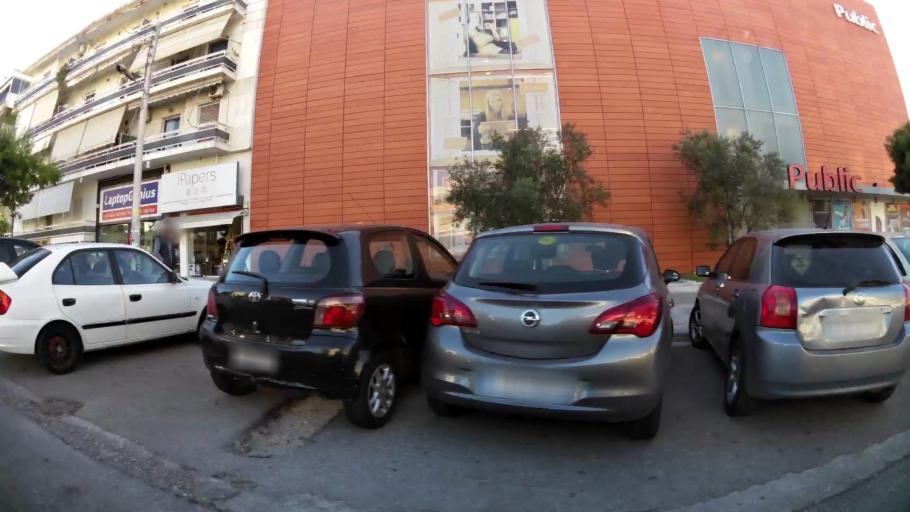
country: GR
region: Attica
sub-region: Nomarchia Athinas
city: Glyfada
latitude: 37.8657
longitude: 23.7454
